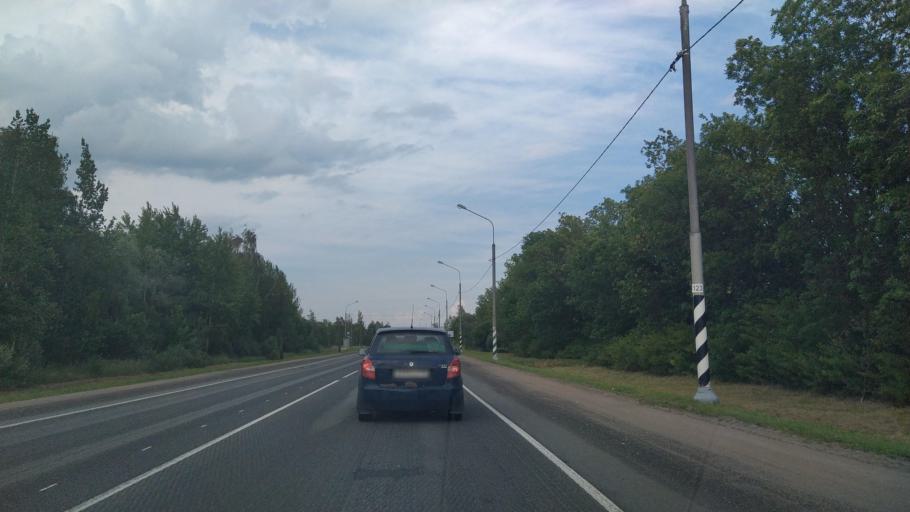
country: RU
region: Novgorod
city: Pankovka
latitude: 58.3841
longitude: 31.0190
